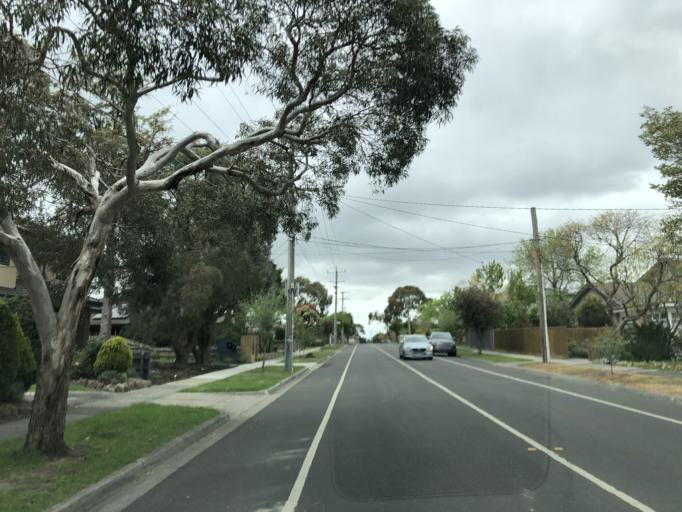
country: AU
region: Victoria
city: Burwood East
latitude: -37.8620
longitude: 145.1357
